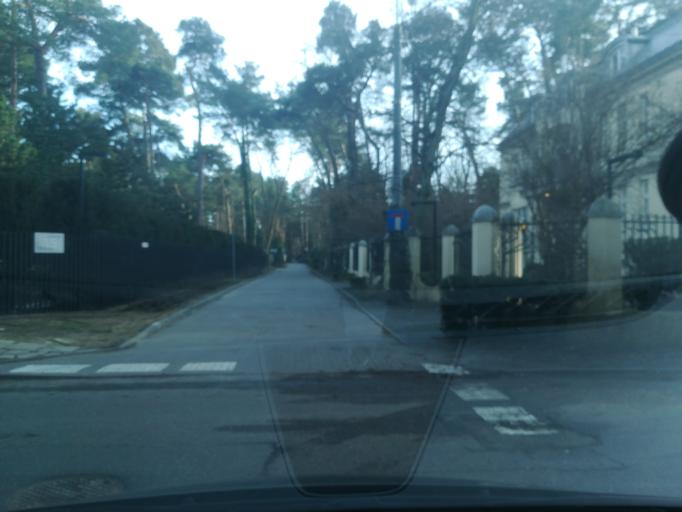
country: PL
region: Masovian Voivodeship
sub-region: Powiat piaseczynski
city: Konstancin-Jeziorna
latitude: 52.0746
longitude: 21.1078
